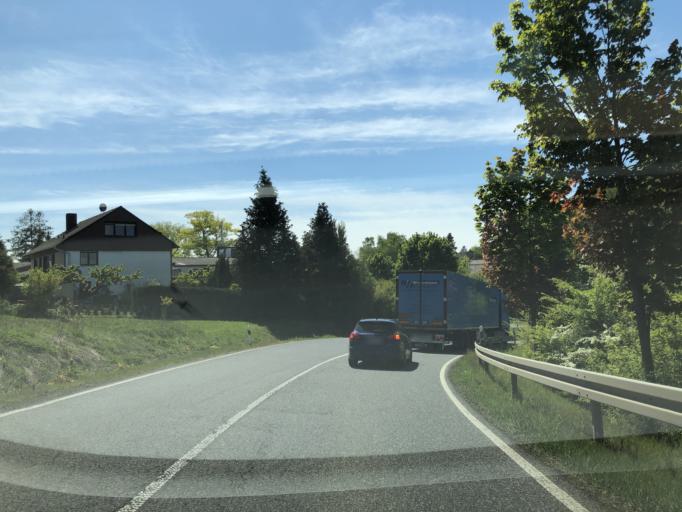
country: DE
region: Hesse
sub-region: Regierungsbezirk Kassel
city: Homberg
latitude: 51.0392
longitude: 9.4131
